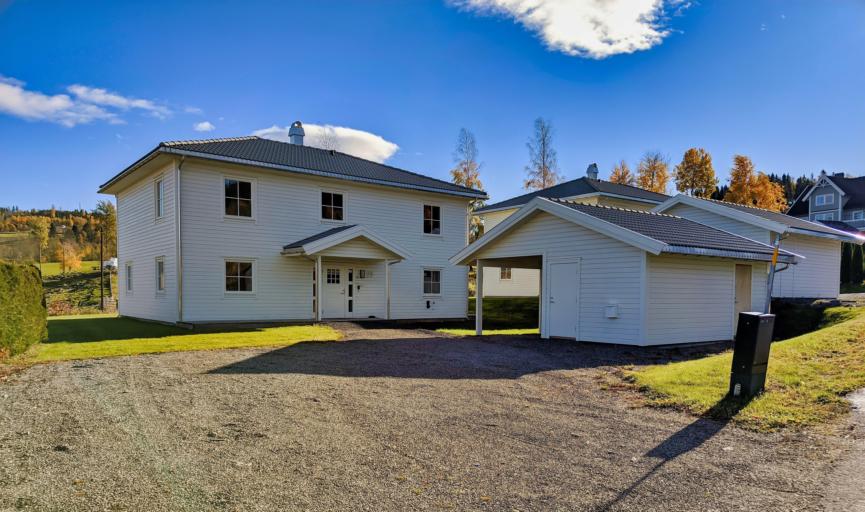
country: NO
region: Hedmark
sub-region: Ringsaker
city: Moelv
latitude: 60.9461
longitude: 10.6105
